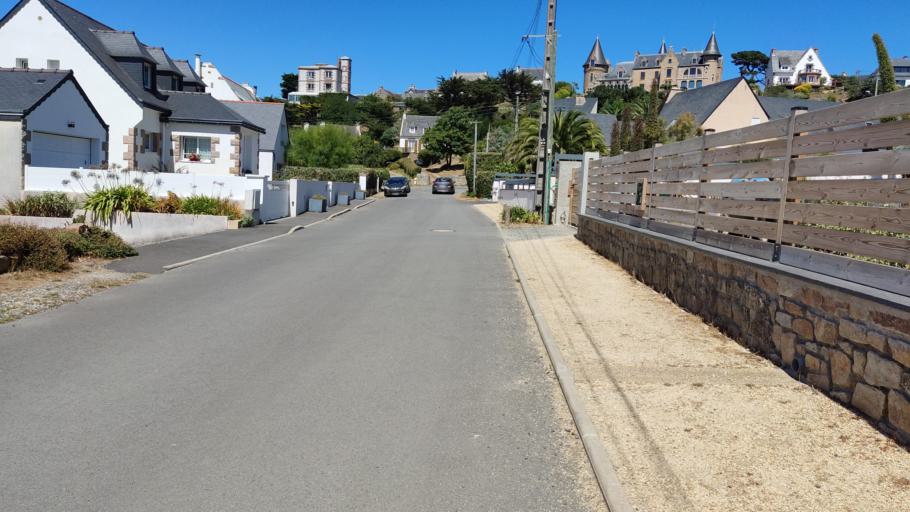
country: FR
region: Brittany
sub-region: Departement des Cotes-d'Armor
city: Trebeurden
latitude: 48.7707
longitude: -3.5818
